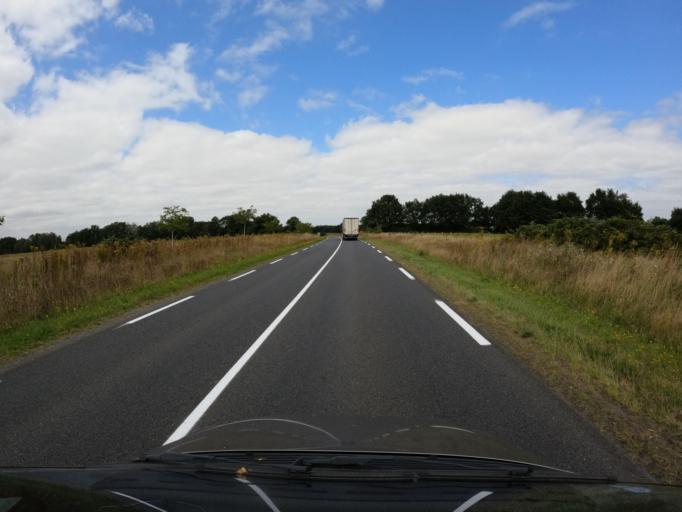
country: FR
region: Poitou-Charentes
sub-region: Departement de la Vienne
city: Charroux
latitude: 46.1456
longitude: 0.4156
